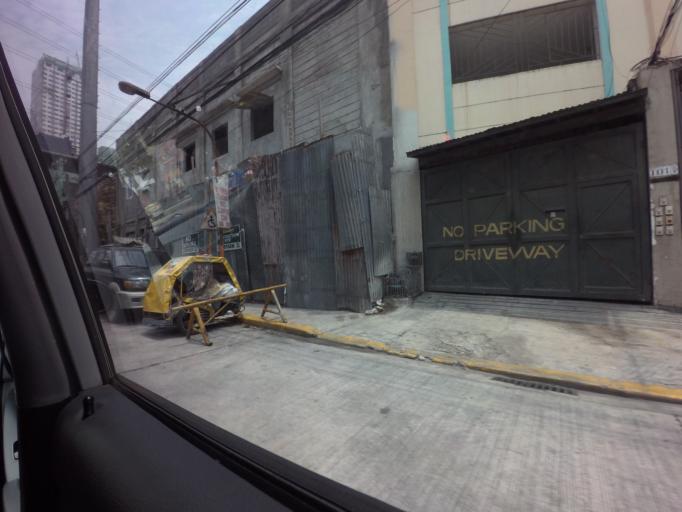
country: PH
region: Metro Manila
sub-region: City of Manila
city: Quiapo
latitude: 14.5799
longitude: 120.9892
